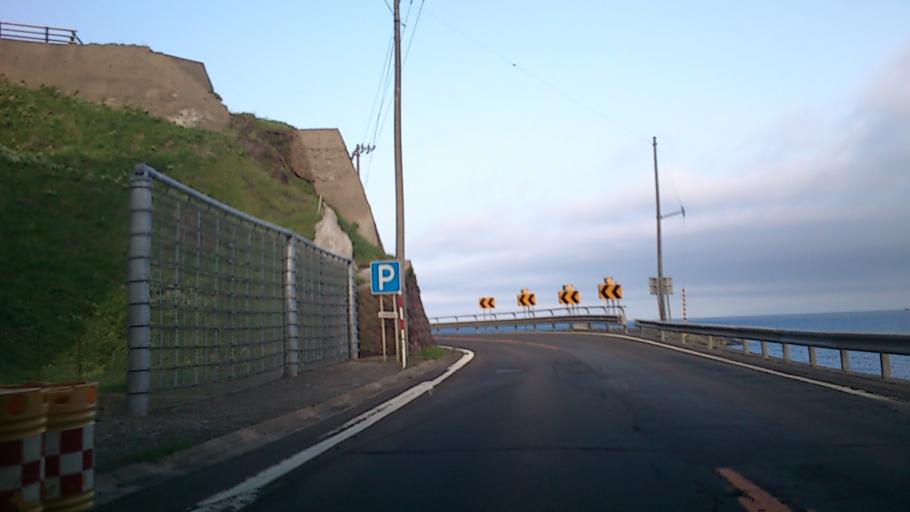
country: JP
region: Aomori
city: Shimokizukuri
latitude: 41.3981
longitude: 140.1965
